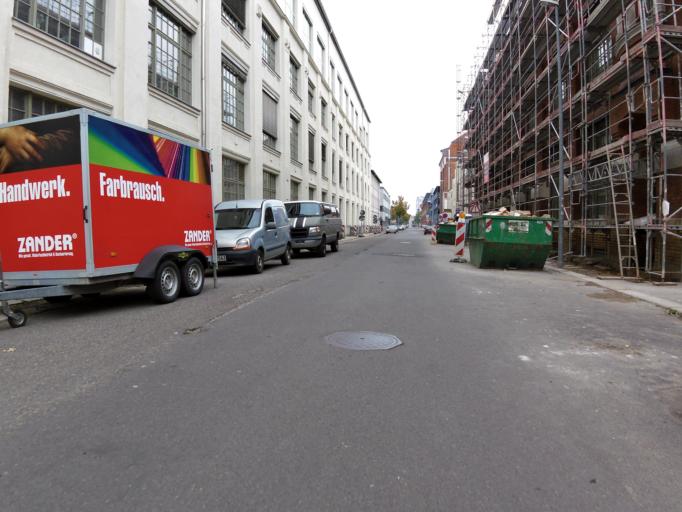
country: DE
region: Saxony
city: Leipzig
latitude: 51.3284
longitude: 12.3261
